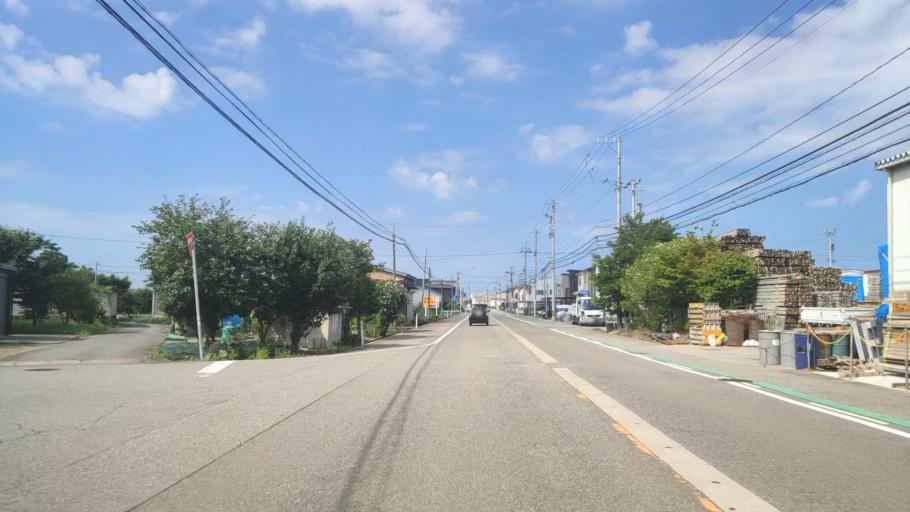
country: JP
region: Ishikawa
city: Tsurugi-asahimachi
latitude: 36.4698
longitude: 136.5963
